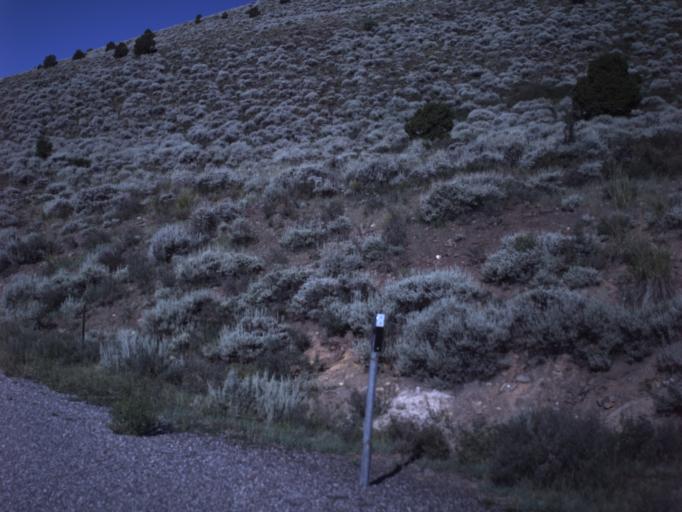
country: US
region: Utah
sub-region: Wayne County
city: Loa
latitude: 38.5925
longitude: -111.4721
